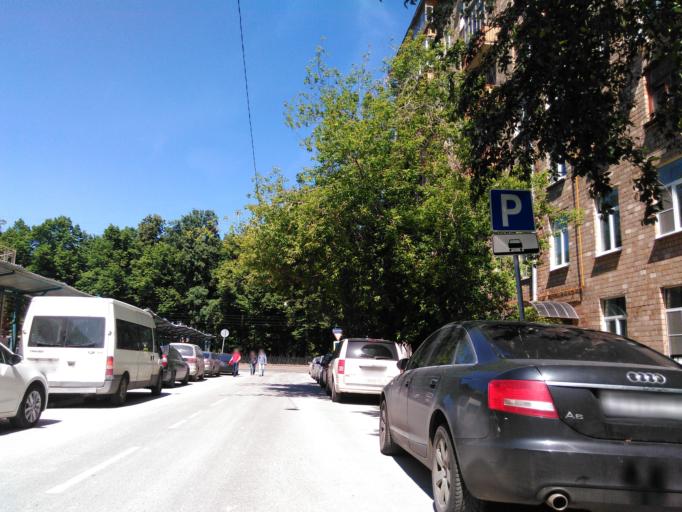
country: RU
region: Moscow
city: Novyye Cheremushki
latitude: 55.7108
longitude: 37.6107
